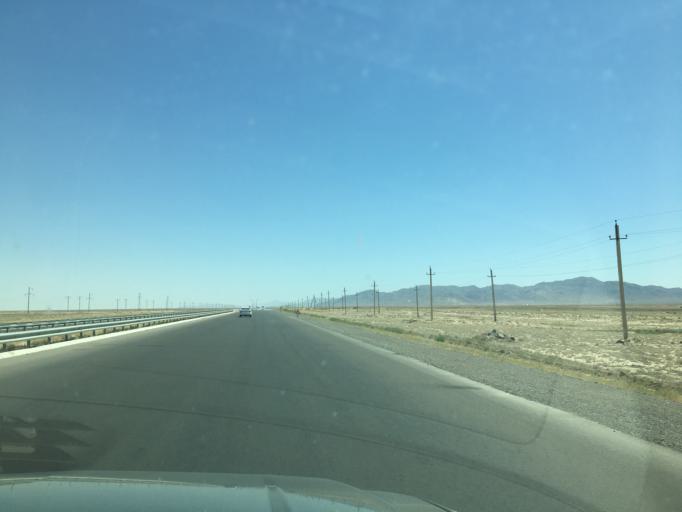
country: TM
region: Balkan
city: Gazanjyk
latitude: 39.1312
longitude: 55.8887
